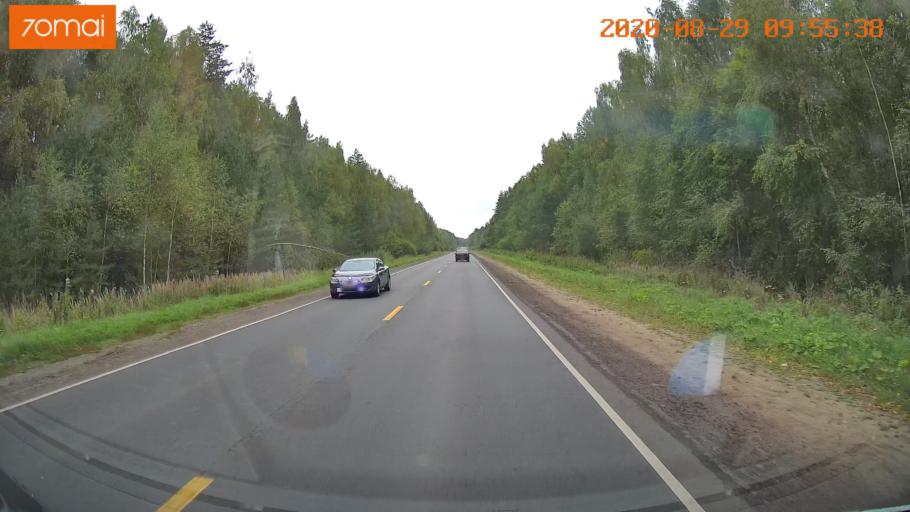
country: RU
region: Ivanovo
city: Zarechnyy
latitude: 57.4220
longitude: 42.2683
